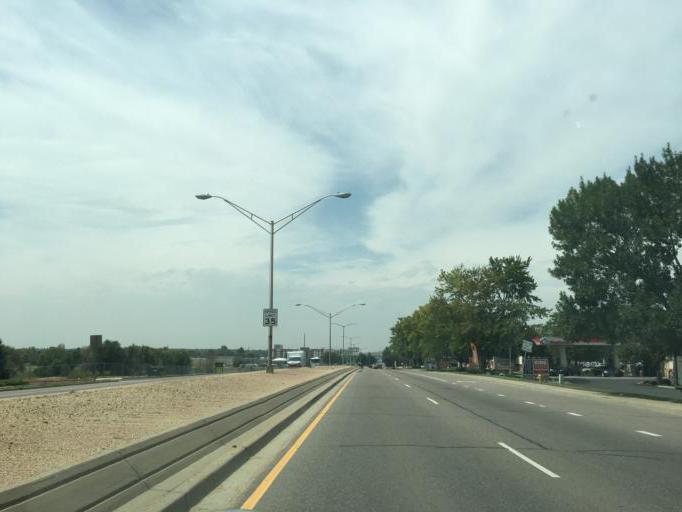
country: US
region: Colorado
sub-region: Adams County
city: Aurora
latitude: 39.7401
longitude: -104.8116
